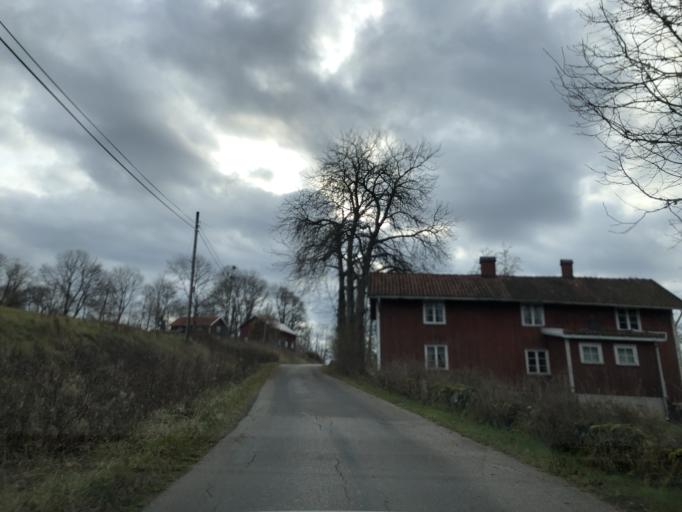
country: SE
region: Vaestra Goetaland
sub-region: Ulricehamns Kommun
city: Ulricehamn
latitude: 57.7228
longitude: 13.3579
